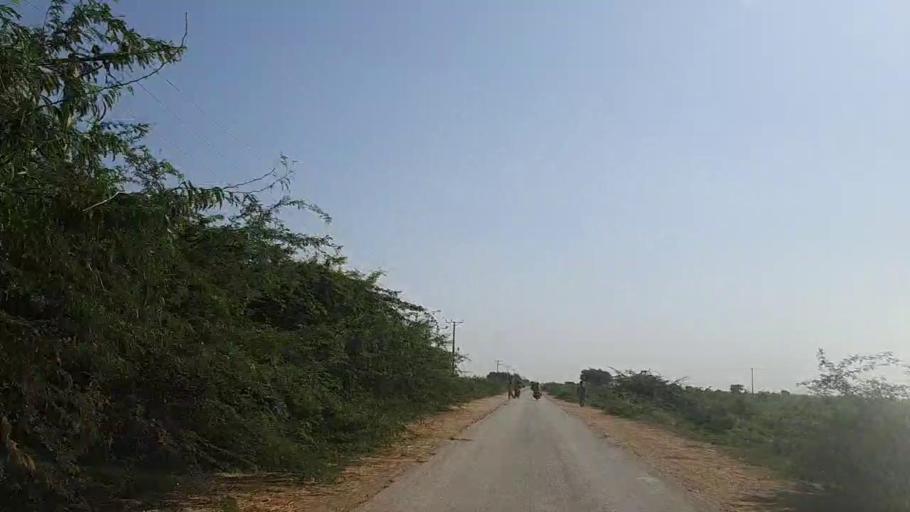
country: PK
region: Sindh
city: Mirpur Batoro
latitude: 24.6380
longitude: 68.2914
